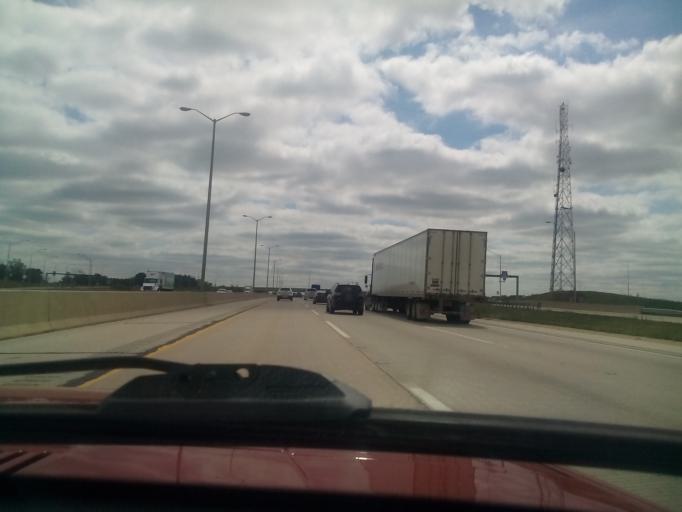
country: US
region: Illinois
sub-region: Cook County
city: Lemont
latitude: 41.6601
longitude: -88.0215
